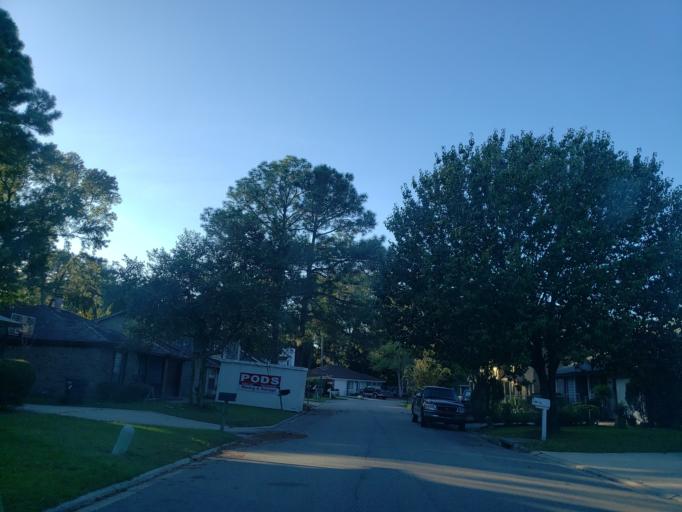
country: US
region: Georgia
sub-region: Chatham County
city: Isle of Hope
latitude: 31.9908
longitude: -81.0715
